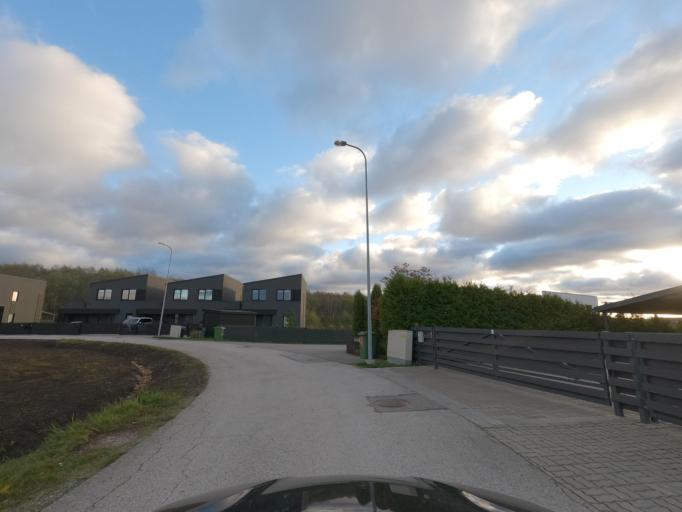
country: EE
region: Harju
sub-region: Kiili vald
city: Kiili
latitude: 59.3648
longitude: 24.8136
